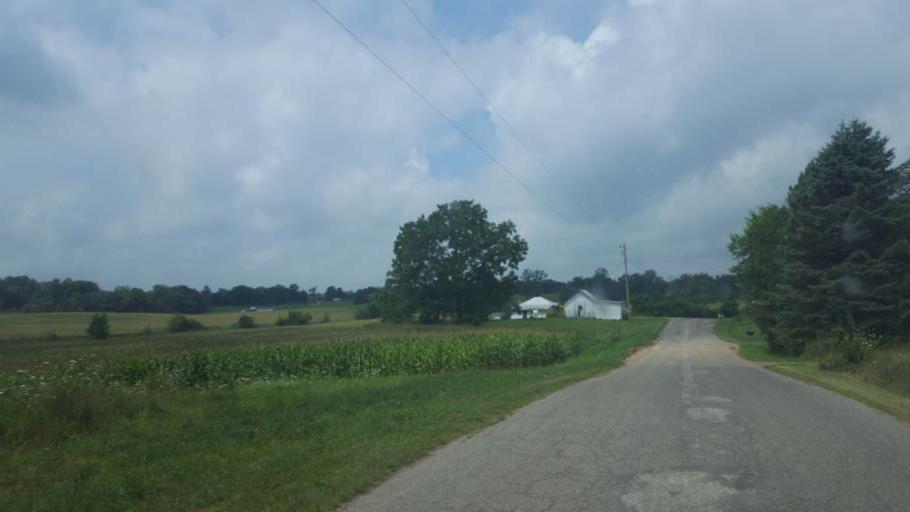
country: US
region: Ohio
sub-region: Morrow County
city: Mount Gilead
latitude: 40.5283
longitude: -82.6935
